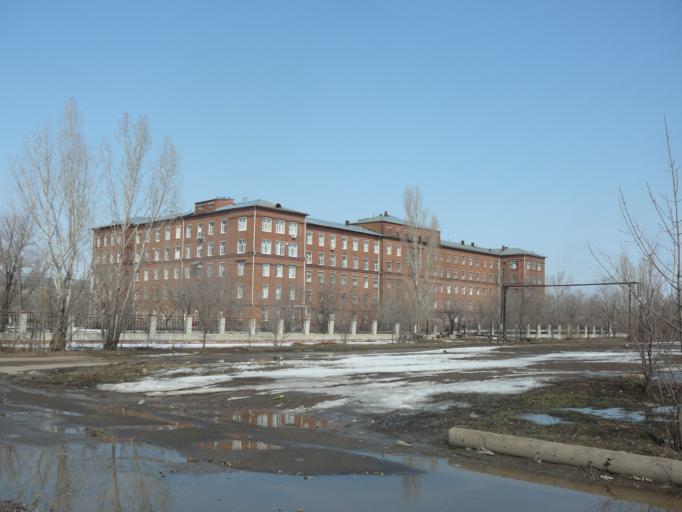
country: RU
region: Saratov
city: Engel's
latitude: 51.4704
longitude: 46.1552
